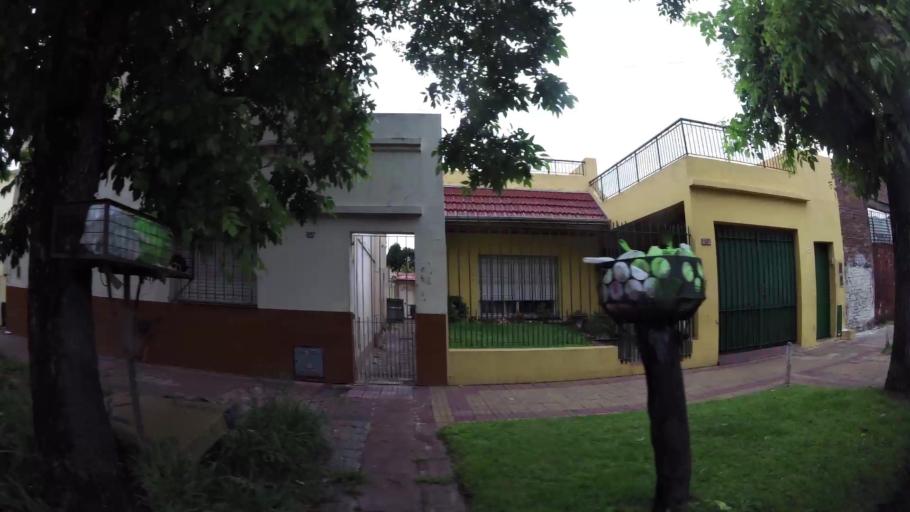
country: AR
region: Buenos Aires
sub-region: Partido de Lanus
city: Lanus
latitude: -34.7215
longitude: -58.3771
